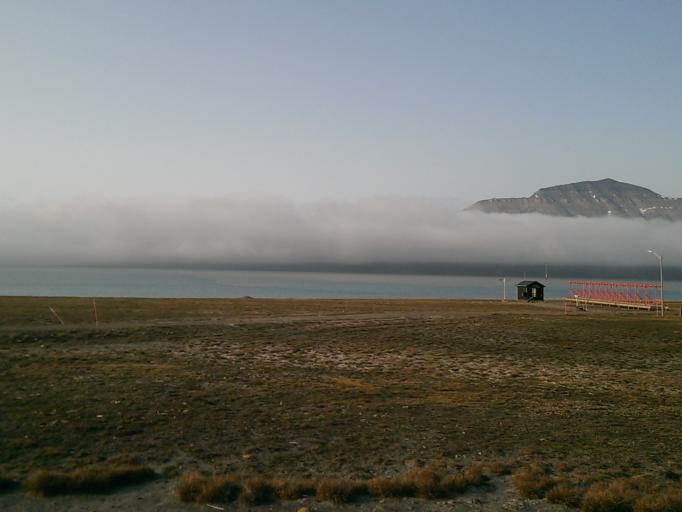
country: SJ
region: Svalbard
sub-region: Spitsbergen
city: Longyearbyen
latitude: 78.2466
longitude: 15.5045
